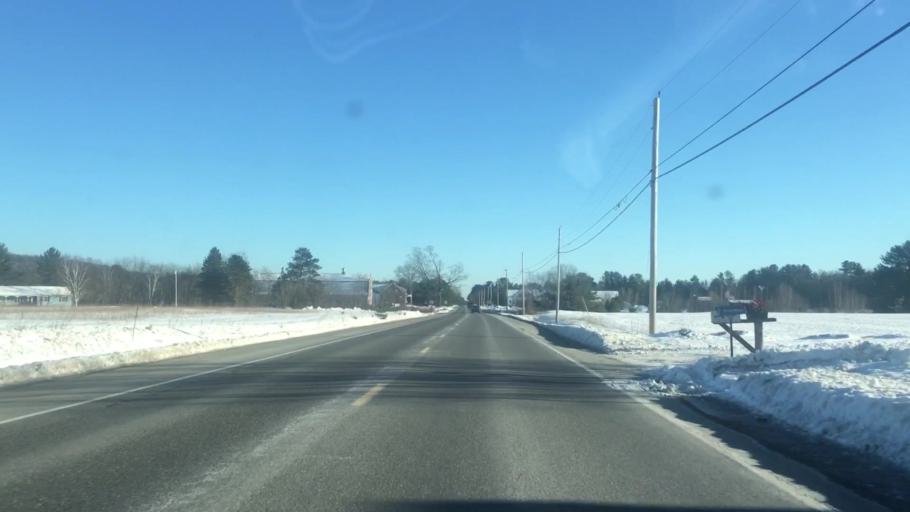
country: US
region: Maine
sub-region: Somerset County
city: Norridgewock
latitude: 44.7093
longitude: -69.7781
